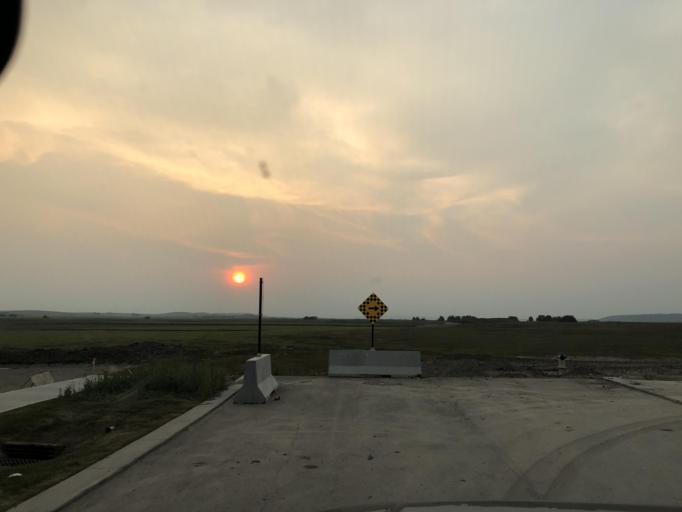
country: CA
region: Alberta
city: Cochrane
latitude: 51.1220
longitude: -114.3932
